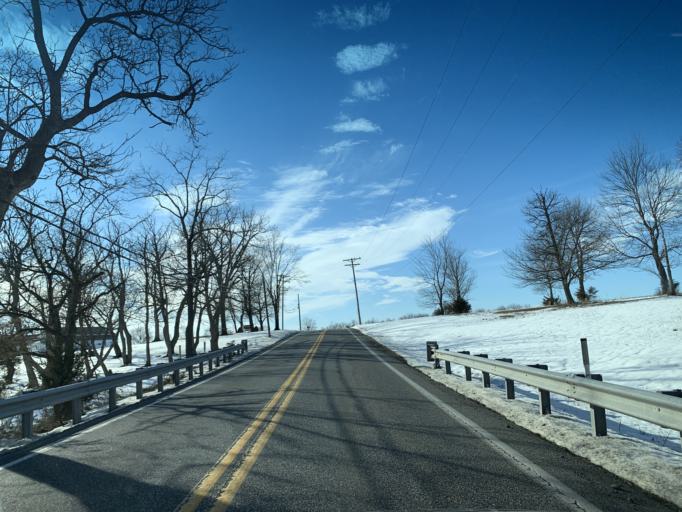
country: US
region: Pennsylvania
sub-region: York County
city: Dillsburg
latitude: 40.0529
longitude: -76.9716
